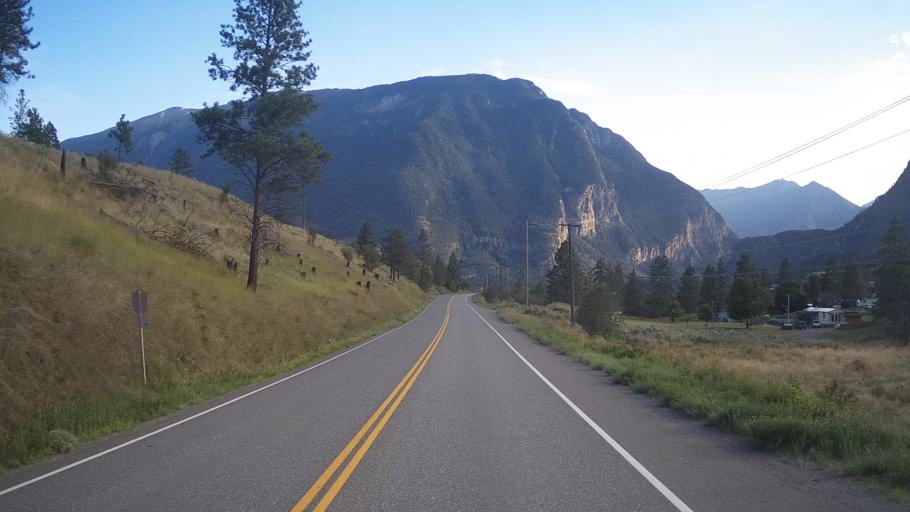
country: CA
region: British Columbia
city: Lillooet
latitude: 50.6967
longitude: -121.9180
